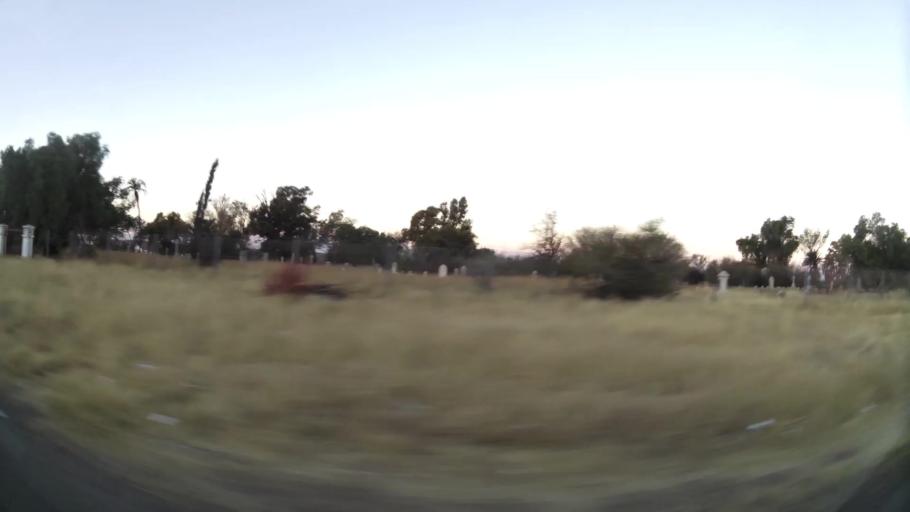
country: ZA
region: Northern Cape
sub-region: Frances Baard District Municipality
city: Kimberley
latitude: -28.7236
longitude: 24.7761
